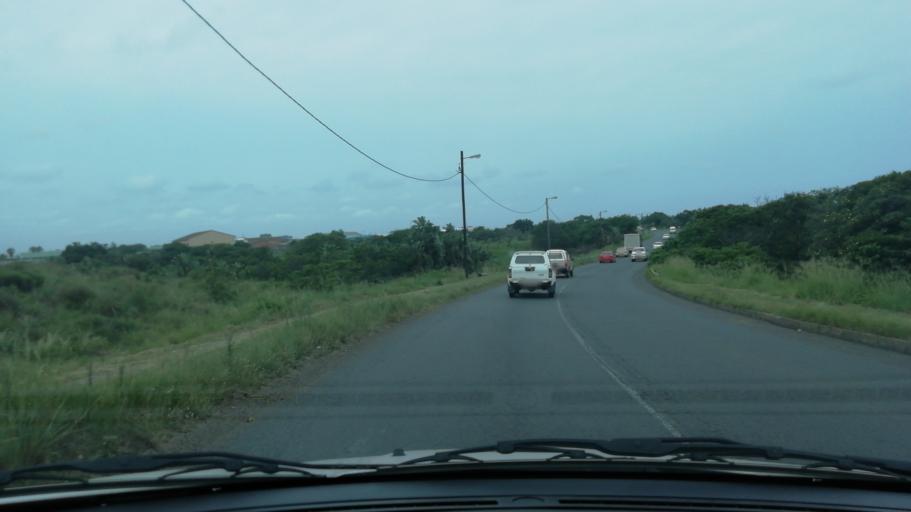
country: ZA
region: KwaZulu-Natal
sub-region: uThungulu District Municipality
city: Richards Bay
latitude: -28.7631
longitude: 32.0389
